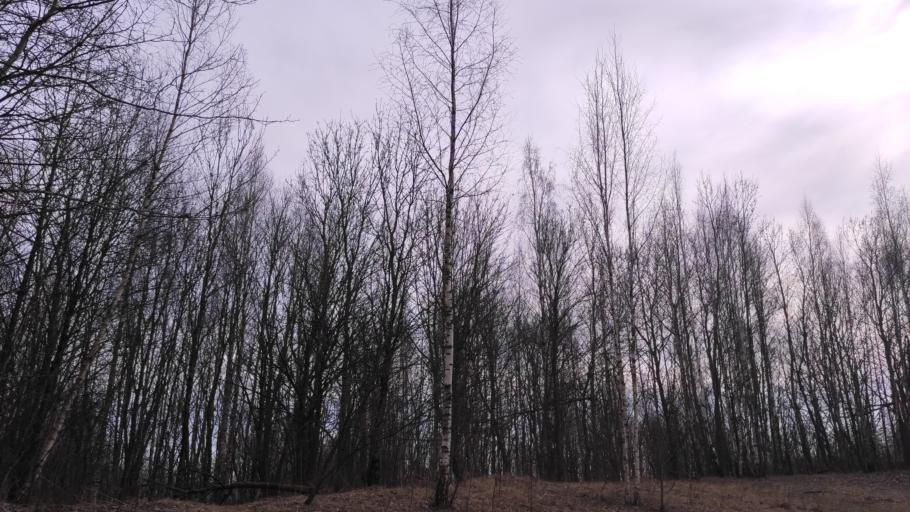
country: BY
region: Minsk
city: Novoye Medvezhino
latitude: 53.8896
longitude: 27.4707
